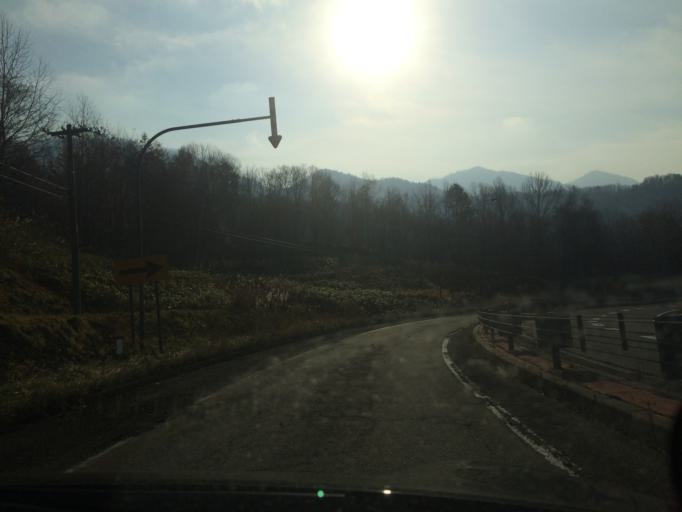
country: JP
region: Hokkaido
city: Shimo-furano
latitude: 42.8821
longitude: 142.2839
